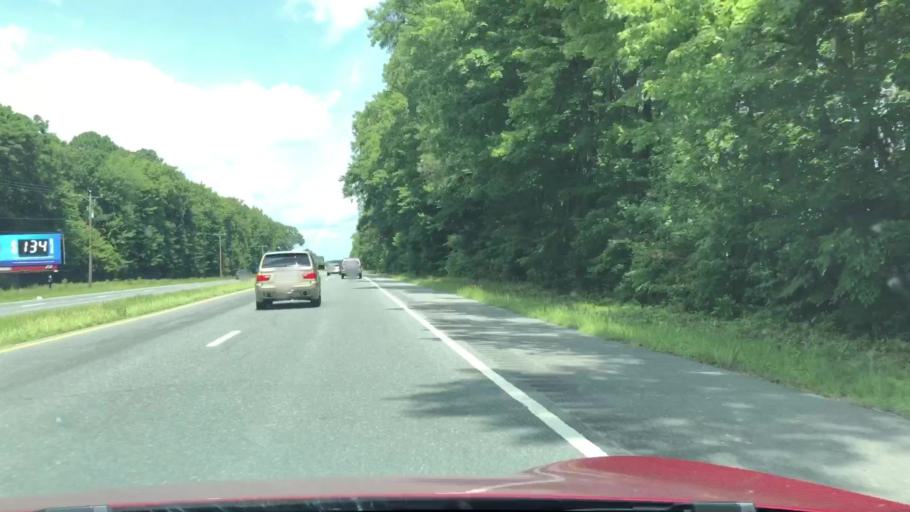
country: US
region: Virginia
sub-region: Northampton County
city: Cape Charles
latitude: 37.1980
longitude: -75.9671
